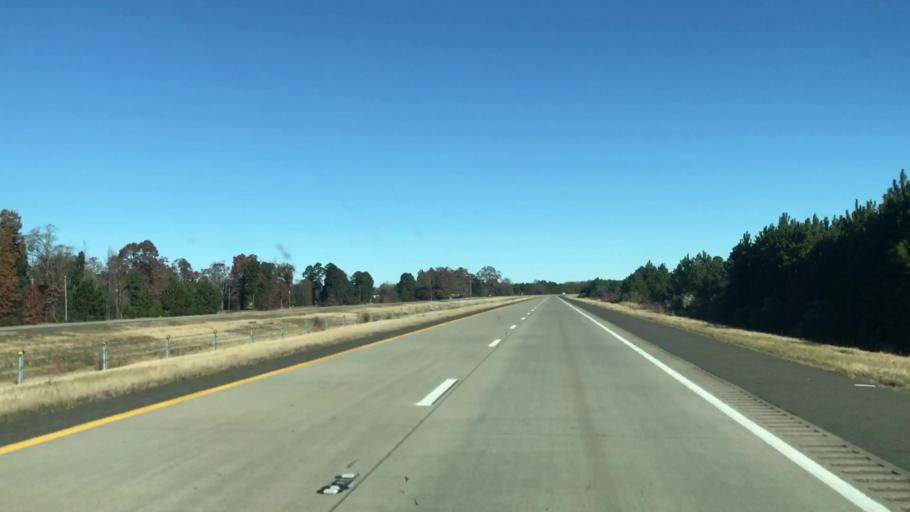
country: US
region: Texas
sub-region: Cass County
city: Queen City
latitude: 33.1939
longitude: -93.8774
